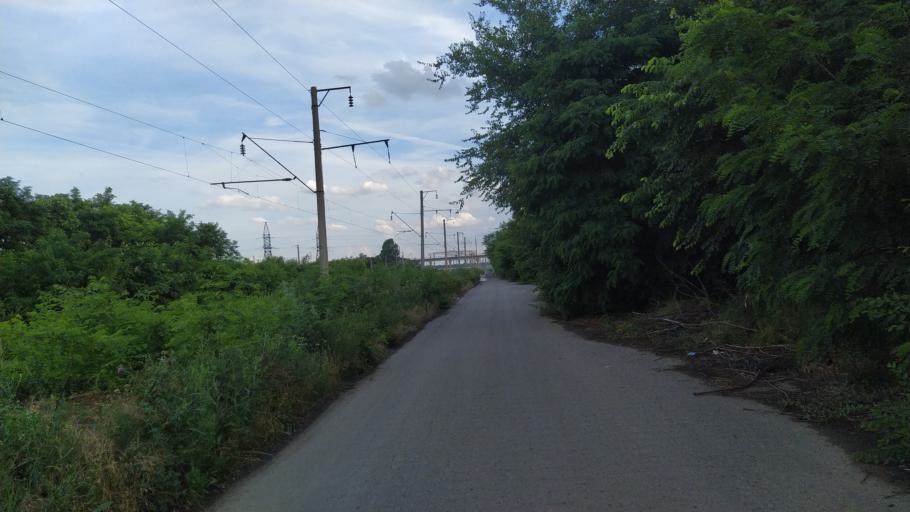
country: RU
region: Rostov
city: Bataysk
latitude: 47.1057
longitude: 39.7121
